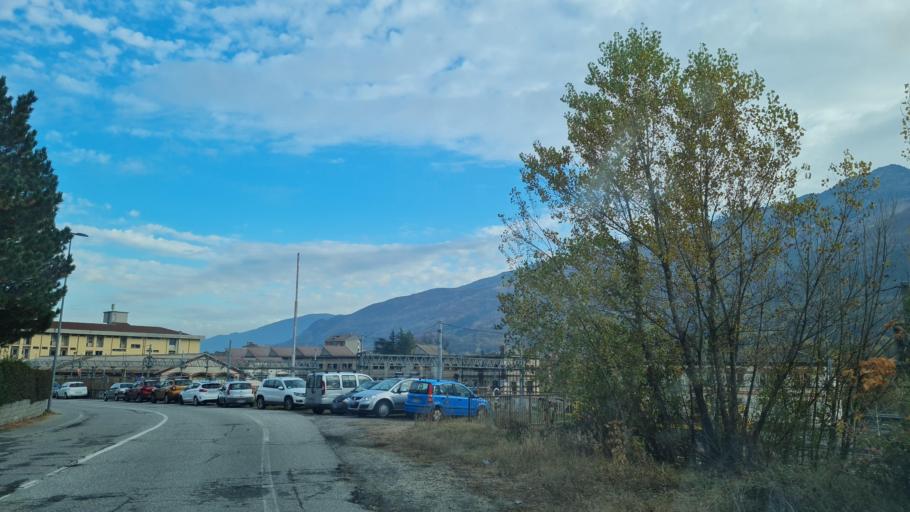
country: IT
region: Piedmont
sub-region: Provincia di Torino
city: Bussoleno
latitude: 45.1397
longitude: 7.1402
